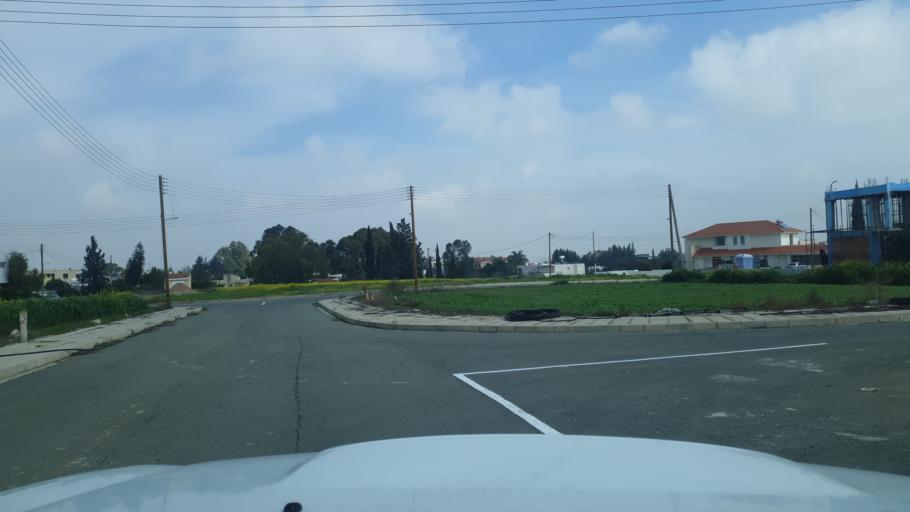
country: CY
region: Lefkosia
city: Kato Deftera
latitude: 35.0834
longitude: 33.2811
